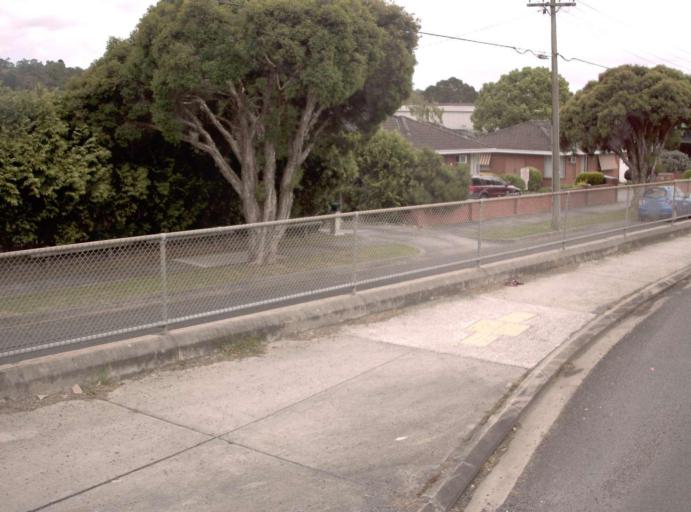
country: AU
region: Victoria
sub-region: Maroondah
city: Croydon North
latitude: -37.7748
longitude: 145.2927
